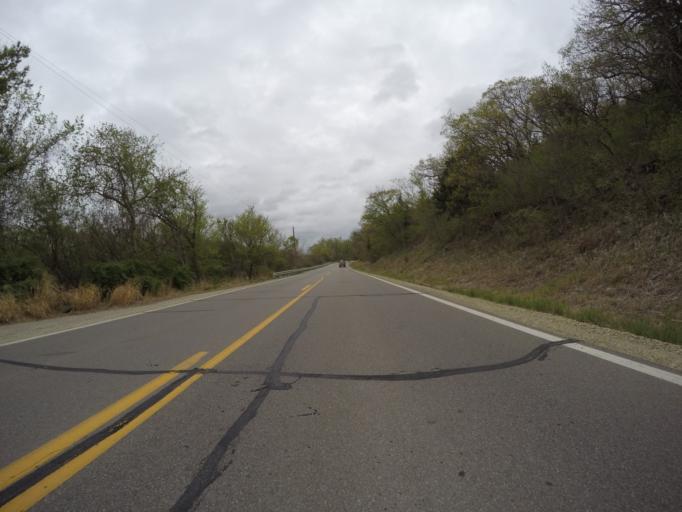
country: US
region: Kansas
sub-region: Riley County
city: Manhattan
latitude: 39.1588
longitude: -96.5566
